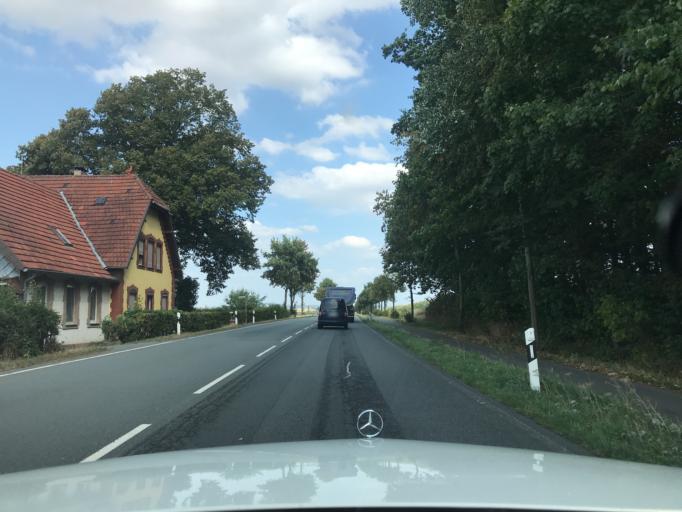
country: DE
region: North Rhine-Westphalia
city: Warburg
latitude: 51.5366
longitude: 9.1711
